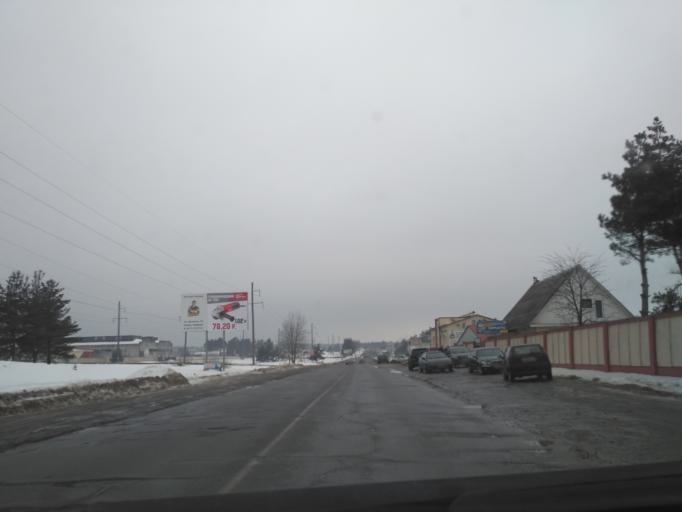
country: BY
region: Minsk
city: Horad Barysaw
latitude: 54.1988
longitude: 28.5033
